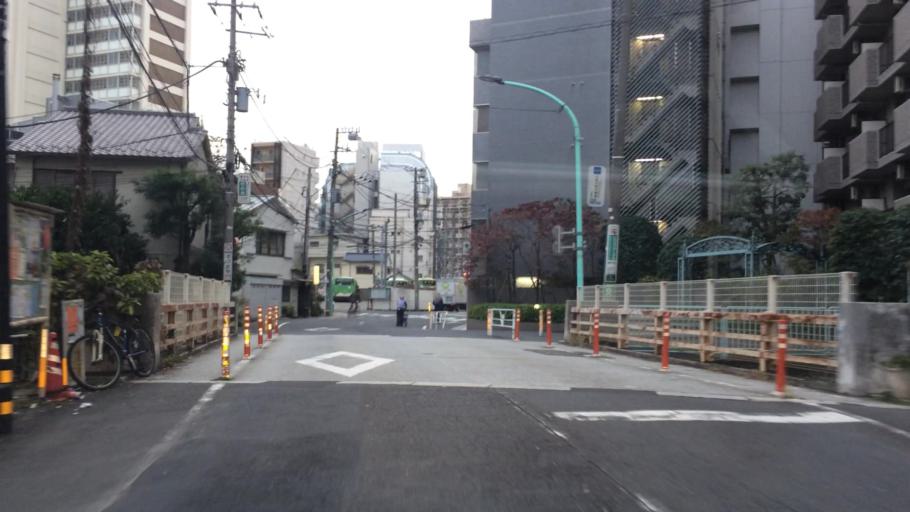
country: JP
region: Tokyo
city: Tokyo
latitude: 35.6539
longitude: 139.7078
